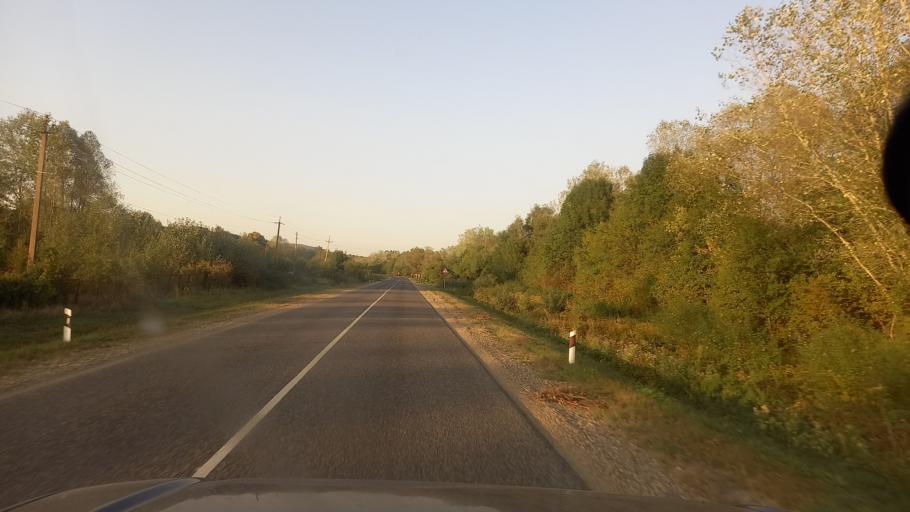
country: RU
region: Krasnodarskiy
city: Smolenskaya
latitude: 44.7554
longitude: 38.7654
